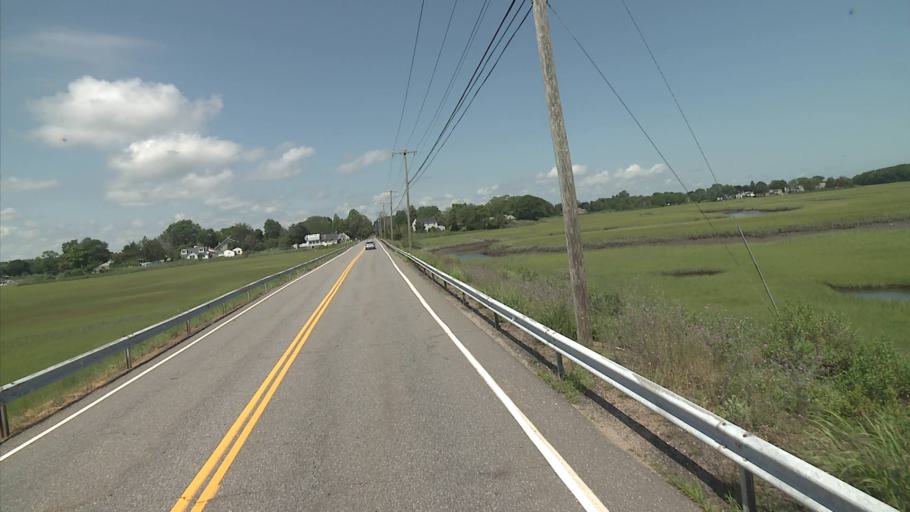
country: US
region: Connecticut
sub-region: Middlesex County
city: Saybrook Manor
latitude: 41.2777
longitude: -72.3932
